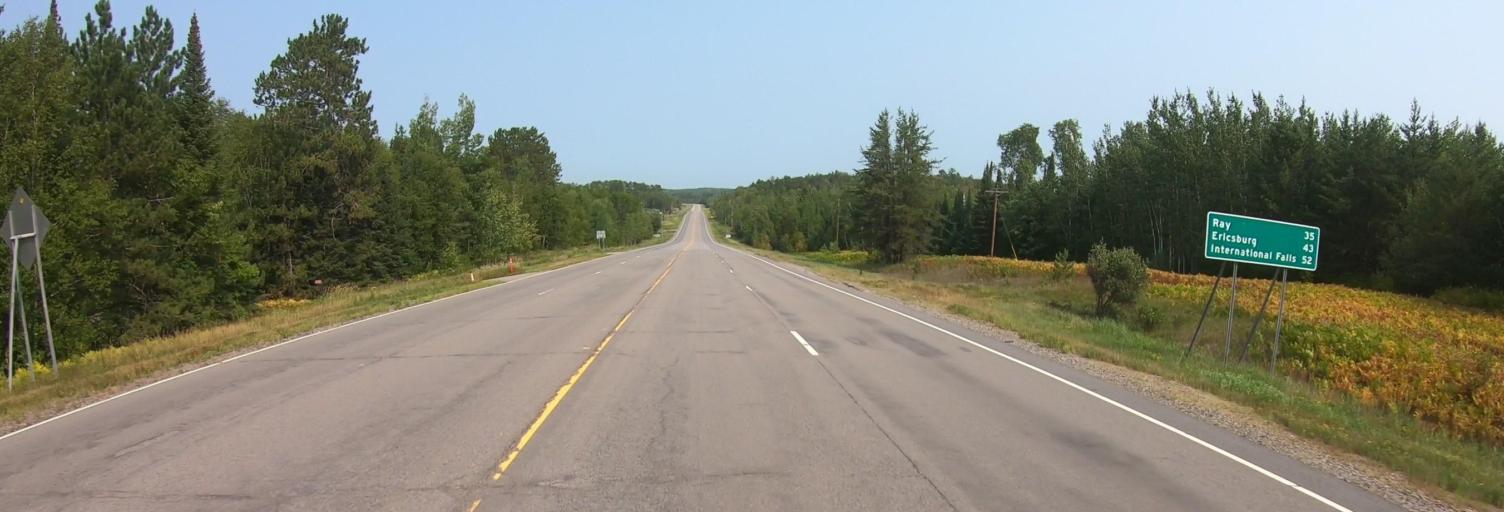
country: US
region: Minnesota
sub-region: Saint Louis County
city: Mountain Iron
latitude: 48.0696
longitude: -92.8226
